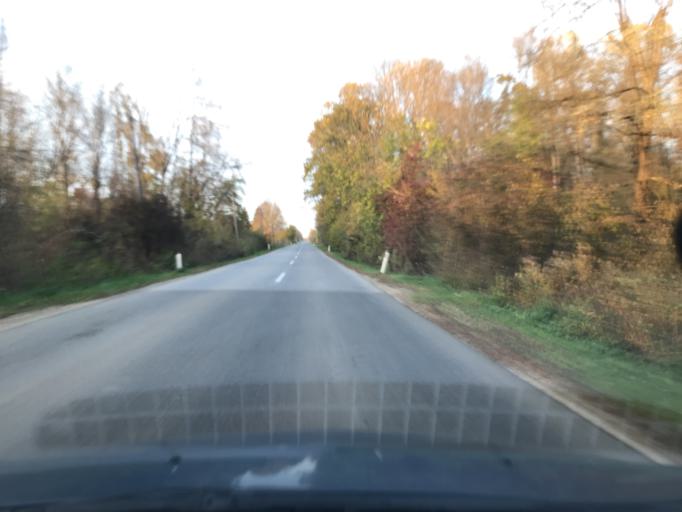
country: BA
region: Republika Srpska
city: Bosanska Dubica
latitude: 45.2324
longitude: 16.9068
